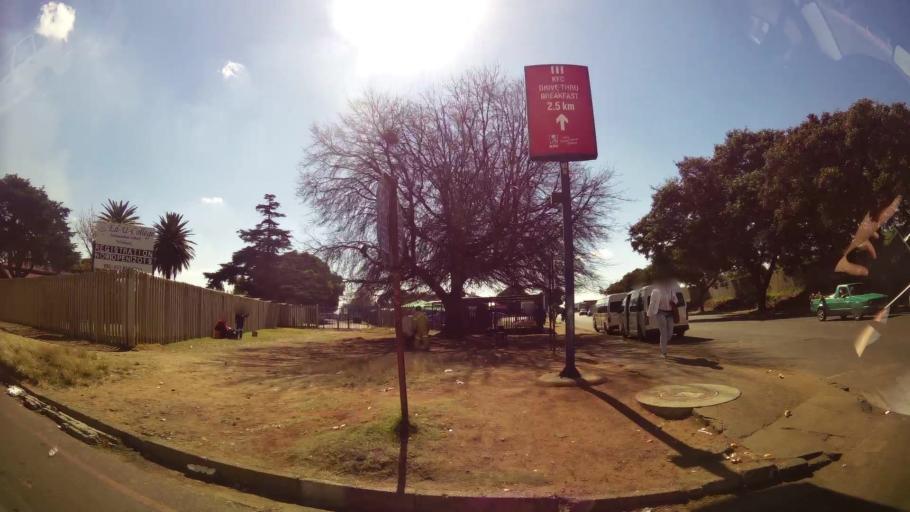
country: ZA
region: Mpumalanga
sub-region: Nkangala District Municipality
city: Witbank
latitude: -25.8723
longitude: 29.2112
